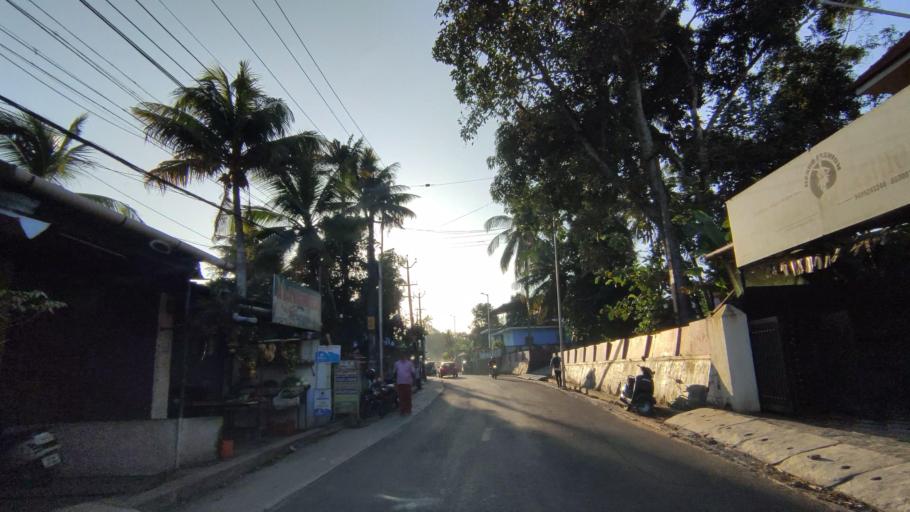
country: IN
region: Kerala
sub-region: Kottayam
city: Kottayam
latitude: 9.6129
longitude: 76.5065
